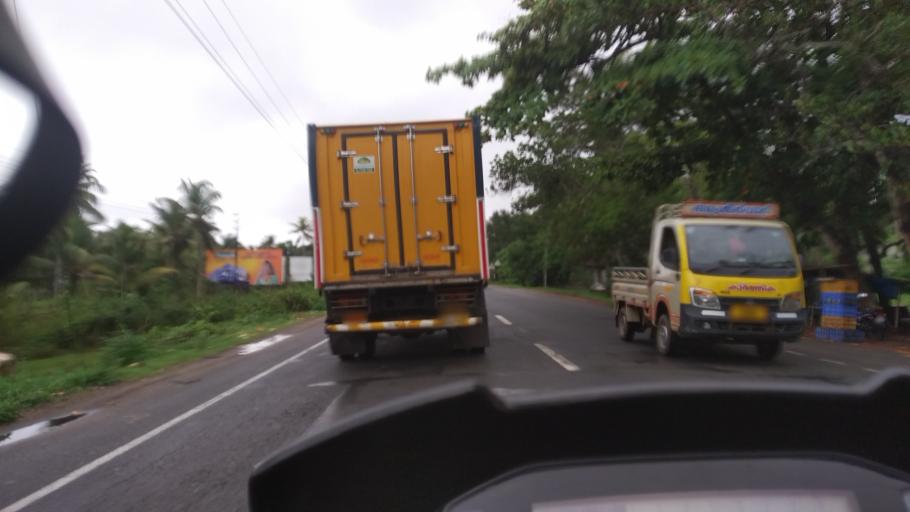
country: IN
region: Kerala
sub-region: Alappuzha
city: Mavelikara
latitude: 9.3162
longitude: 76.4125
